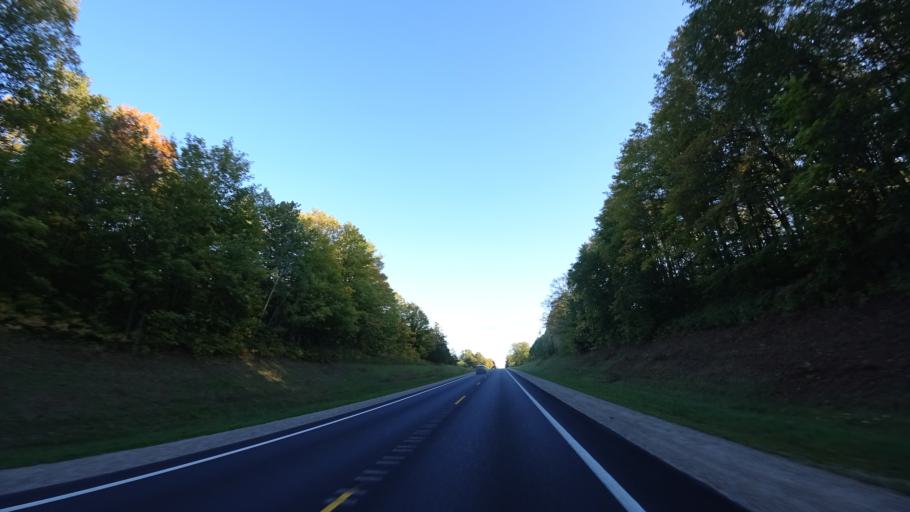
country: US
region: Michigan
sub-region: Luce County
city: Newberry
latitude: 46.3270
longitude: -85.6727
